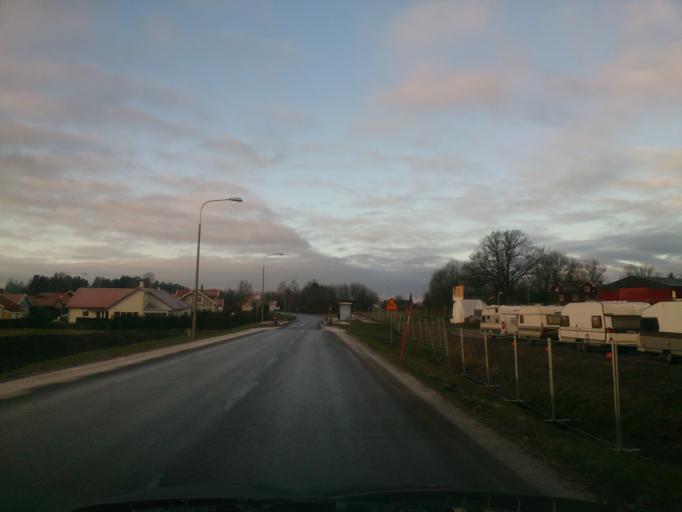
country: SE
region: OEstergoetland
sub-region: Linkopings Kommun
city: Linghem
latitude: 58.4080
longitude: 15.8563
